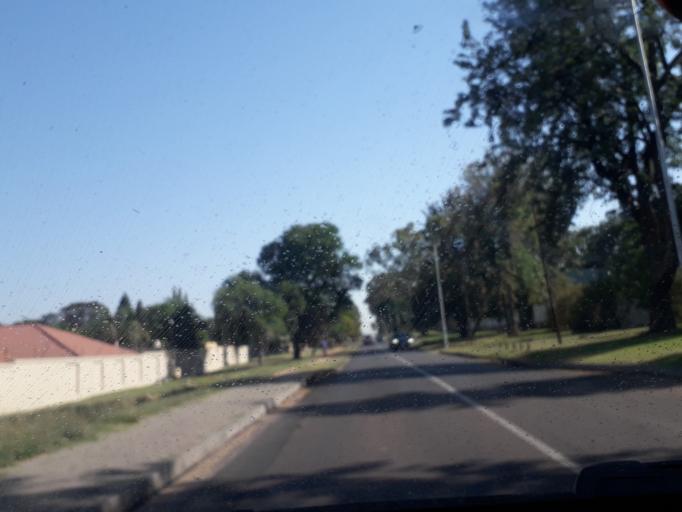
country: ZA
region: Gauteng
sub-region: City of Johannesburg Metropolitan Municipality
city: Midrand
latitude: -26.0302
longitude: 28.0699
